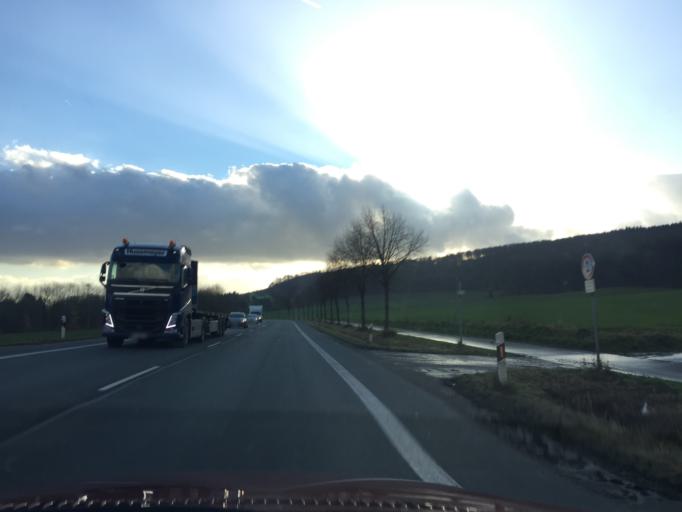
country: DE
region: North Rhine-Westphalia
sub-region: Regierungsbezirk Detmold
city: Hoexter
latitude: 51.8102
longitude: 9.4011
